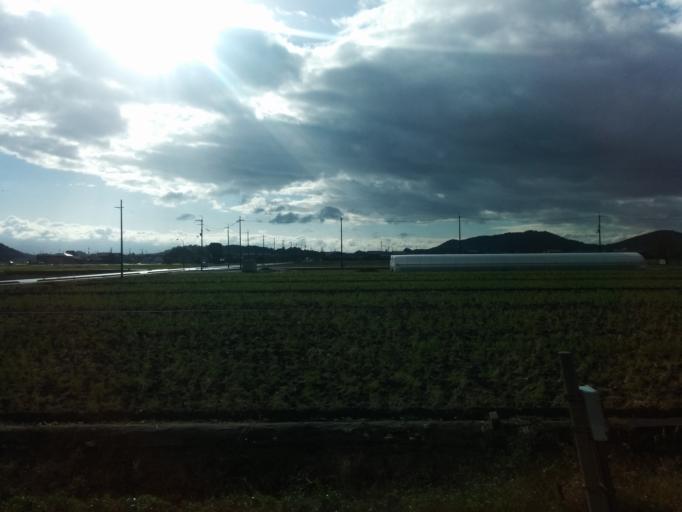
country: JP
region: Shiga Prefecture
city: Omihachiman
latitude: 35.1348
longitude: 136.1201
